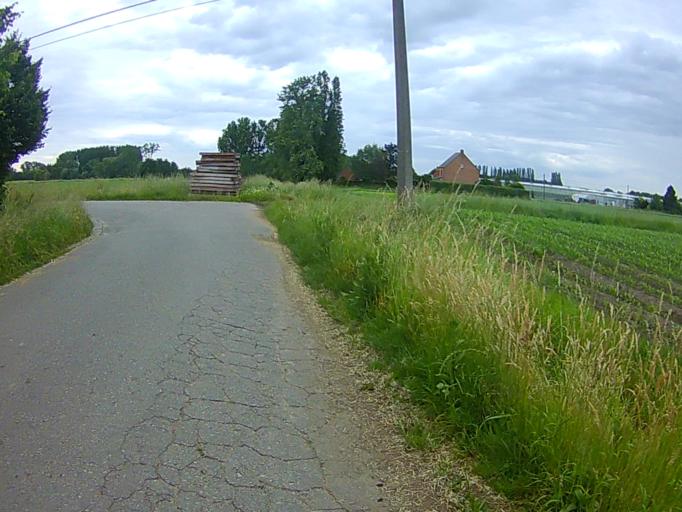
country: BE
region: Flanders
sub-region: Provincie Antwerpen
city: Putte
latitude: 51.0695
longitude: 4.6376
